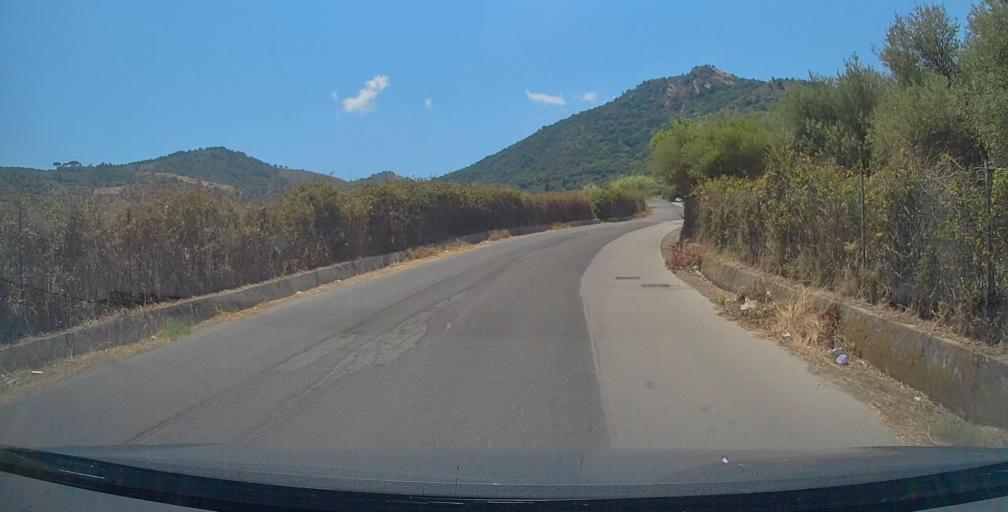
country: IT
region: Sicily
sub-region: Messina
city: Oliveri
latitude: 38.1435
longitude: 15.0155
